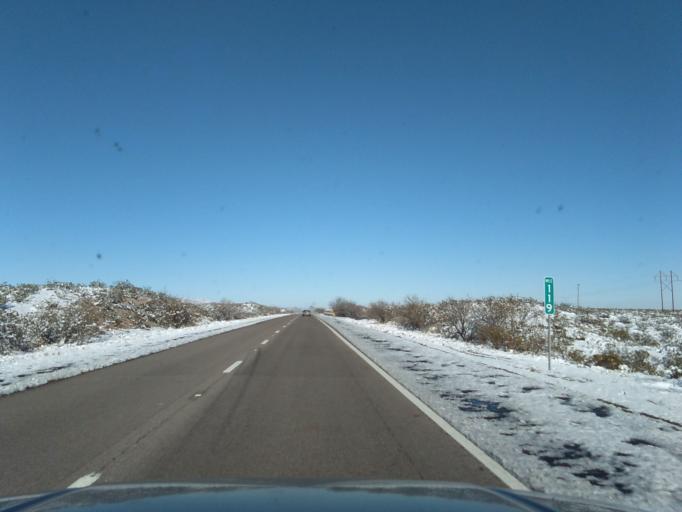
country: US
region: New Mexico
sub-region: Socorro County
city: Socorro
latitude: 33.6755
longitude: -107.0759
